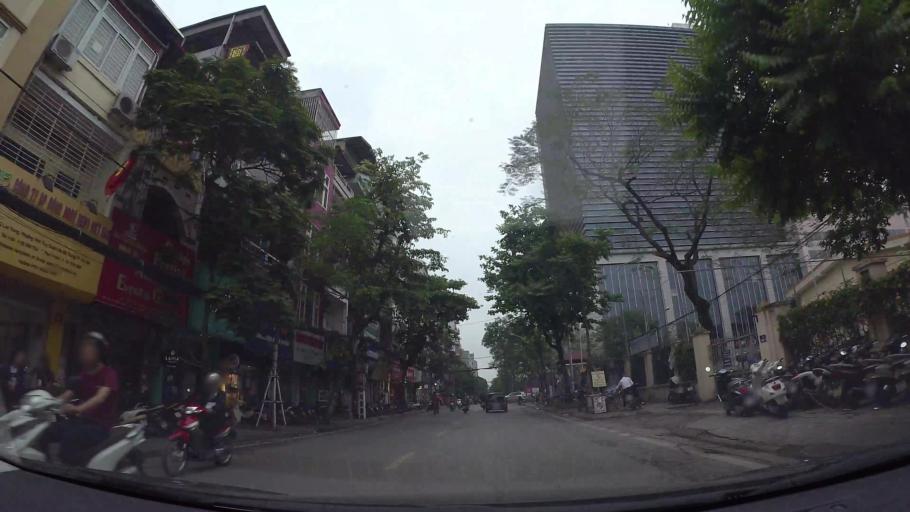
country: VN
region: Ha Noi
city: Hai BaTrung
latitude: 21.0030
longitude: 105.8632
